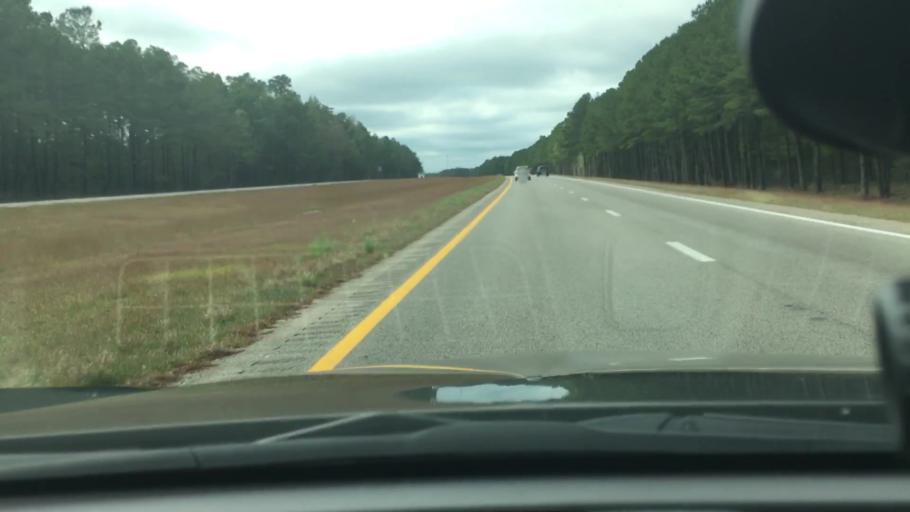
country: US
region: North Carolina
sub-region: Nash County
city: Spring Hope
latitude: 35.7860
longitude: -78.1004
